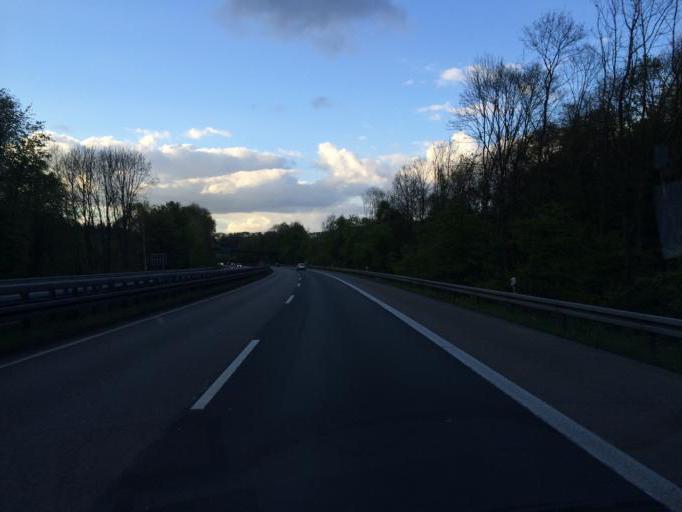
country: DE
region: North Rhine-Westphalia
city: Sprockhovel
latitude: 51.3653
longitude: 7.2756
